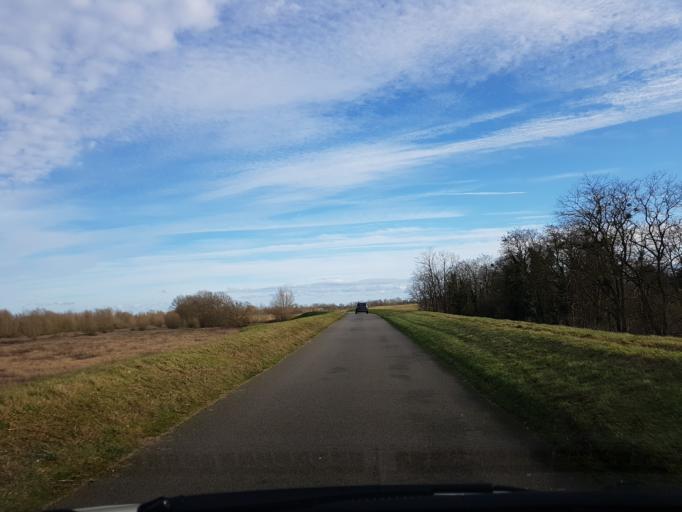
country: FR
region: Centre
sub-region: Departement du Loiret
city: Checy
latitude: 47.8843
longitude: 2.0074
